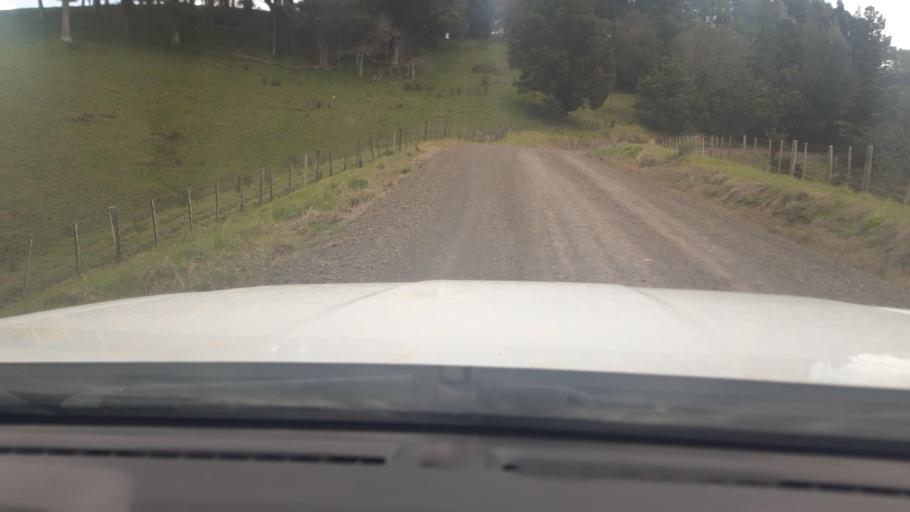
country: NZ
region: Northland
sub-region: Far North District
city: Kaitaia
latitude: -35.0823
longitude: 173.3214
